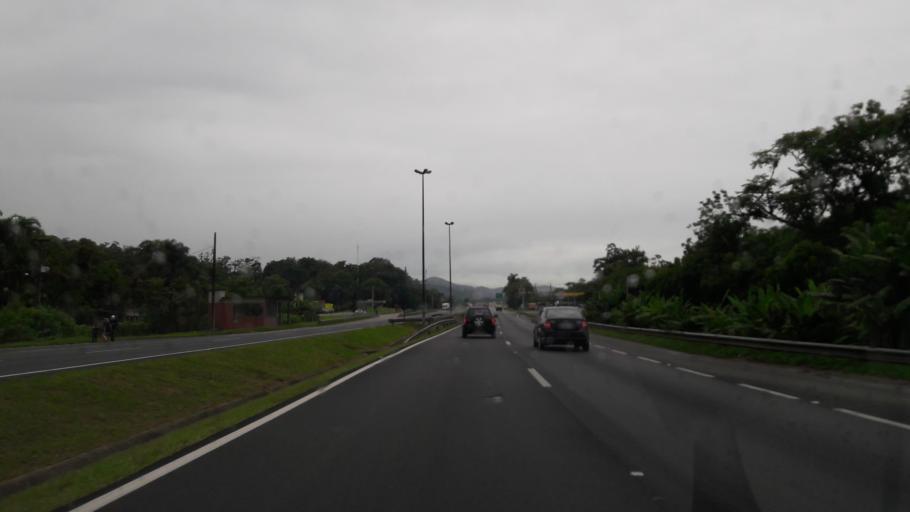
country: BR
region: Parana
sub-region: Antonina
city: Antonina
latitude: -25.5528
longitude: -48.8000
